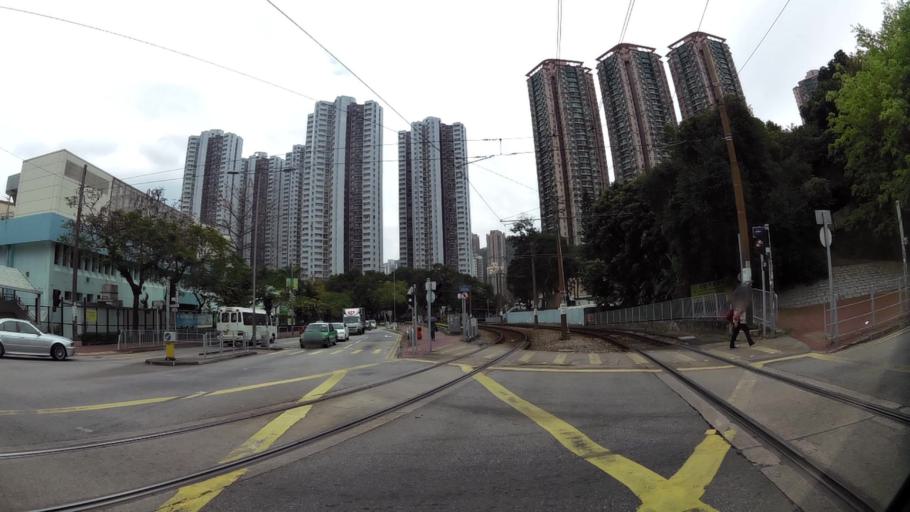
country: HK
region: Tuen Mun
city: Tuen Mun
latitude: 22.4028
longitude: 113.9729
